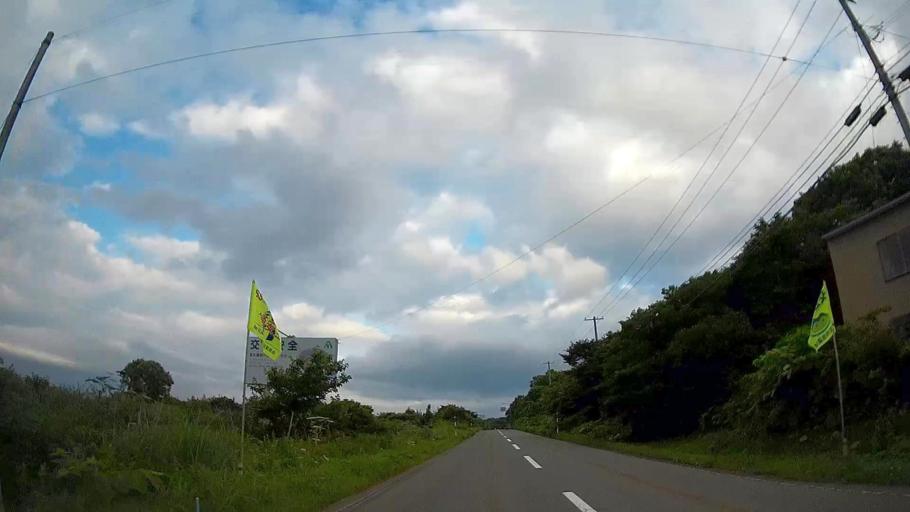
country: JP
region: Hokkaido
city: Nanae
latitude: 42.1190
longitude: 140.7432
